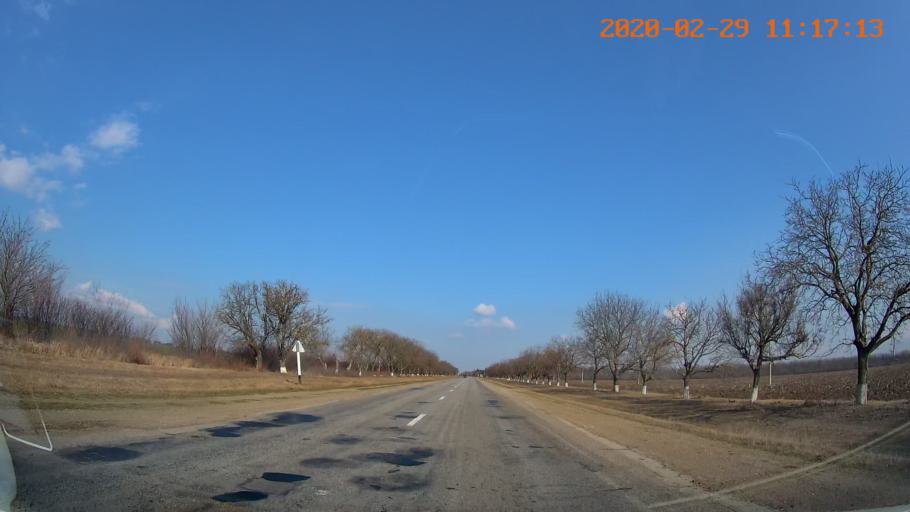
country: MD
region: Telenesti
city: Dubasari
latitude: 47.3192
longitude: 29.1700
